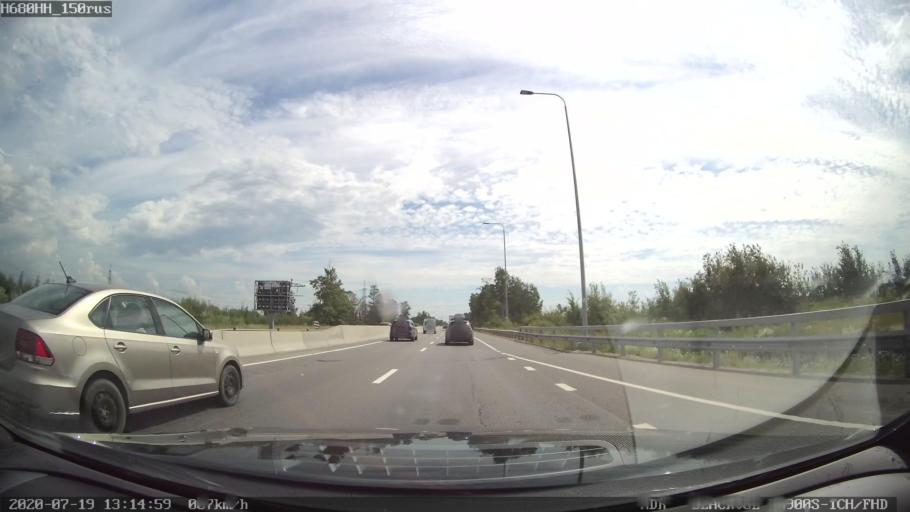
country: RU
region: St.-Petersburg
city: Kolpino
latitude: 59.7290
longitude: 30.5330
